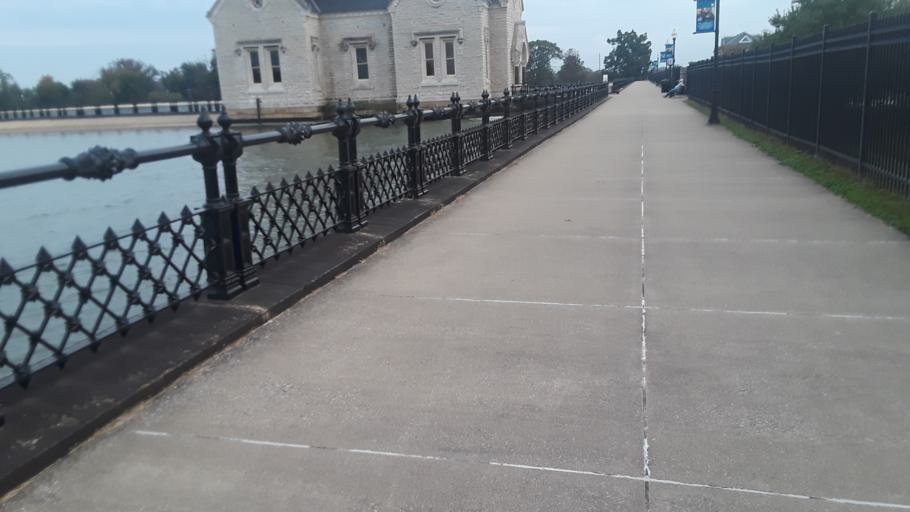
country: US
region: Kentucky
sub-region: Jefferson County
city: Indian Hills
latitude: 38.2574
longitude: -85.6801
